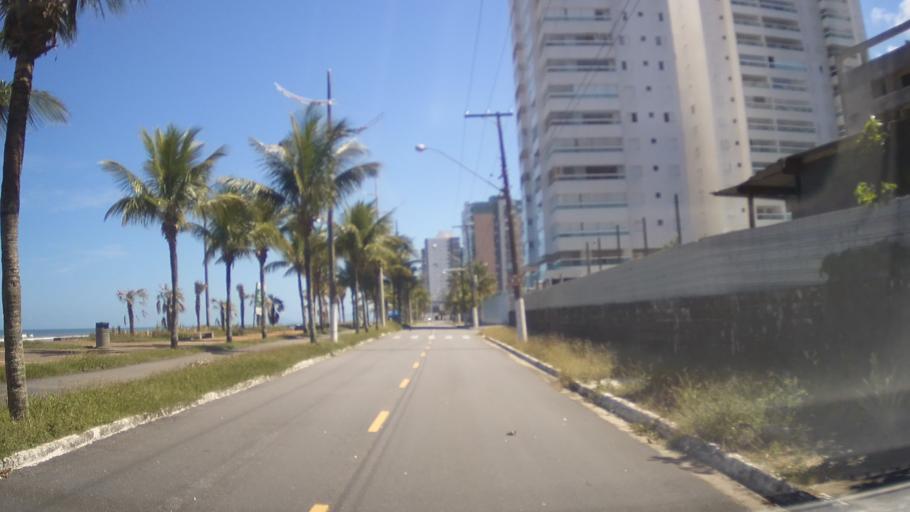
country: BR
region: Sao Paulo
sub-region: Mongagua
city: Mongagua
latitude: -24.0878
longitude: -46.6035
